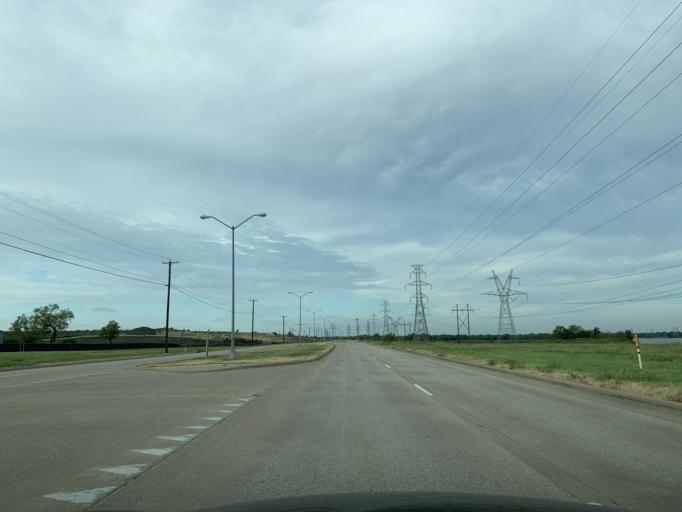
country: US
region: Texas
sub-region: Dallas County
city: Grand Prairie
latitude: 32.7028
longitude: -96.9568
